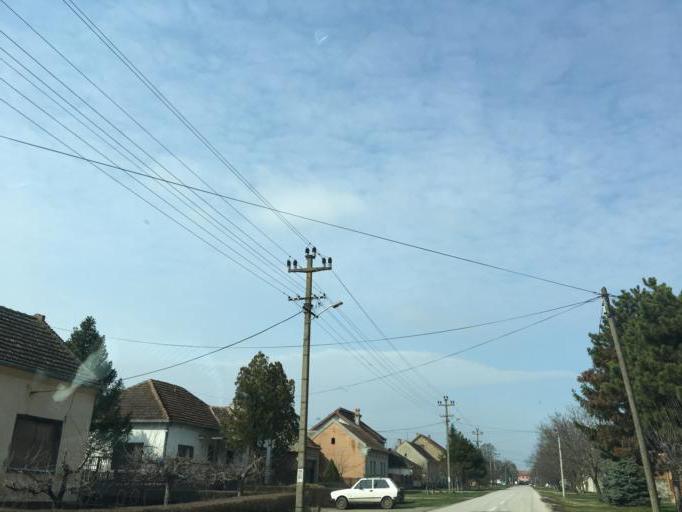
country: RS
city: Centa
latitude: 45.1047
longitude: 20.3920
